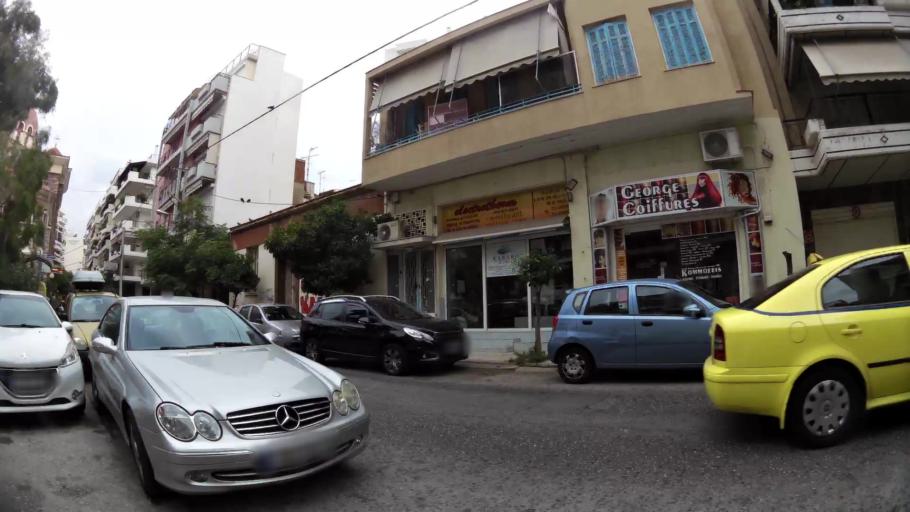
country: GR
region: Attica
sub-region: Nomos Attikis
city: Piraeus
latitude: 37.9296
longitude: 23.6356
